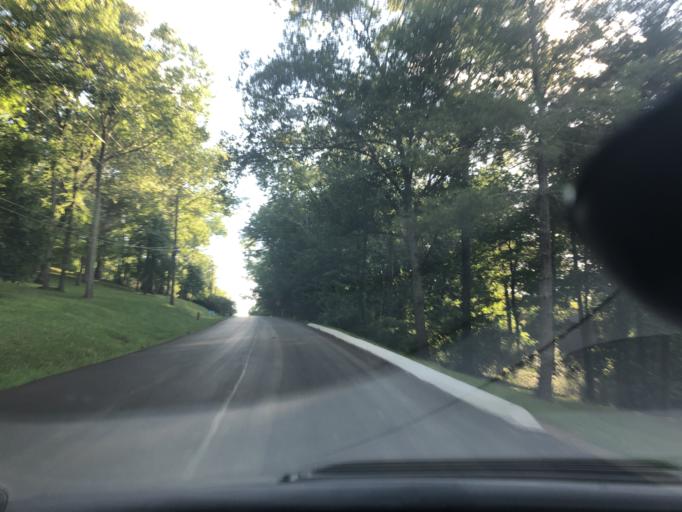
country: US
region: Tennessee
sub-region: Davidson County
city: Forest Hills
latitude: 36.0577
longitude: -86.8385
